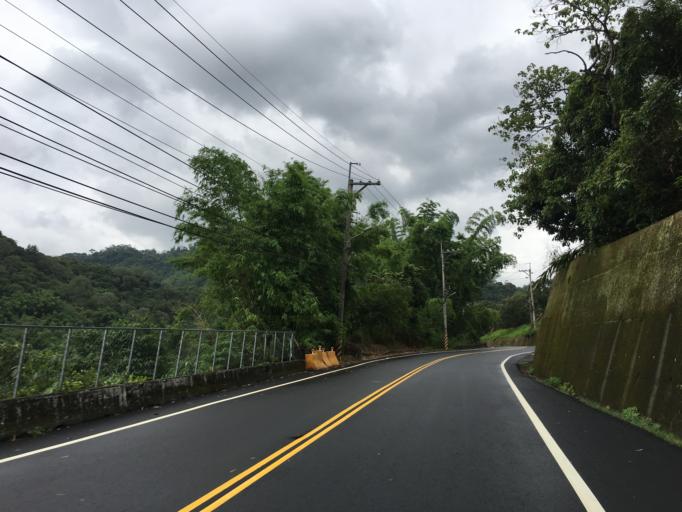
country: TW
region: Taiwan
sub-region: Taichung City
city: Taichung
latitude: 24.0726
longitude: 120.7295
